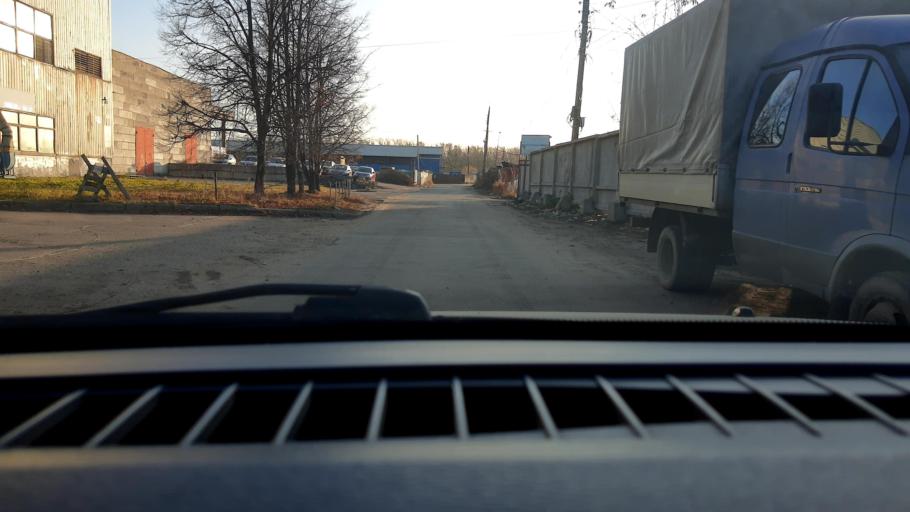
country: RU
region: Nizjnij Novgorod
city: Gorbatovka
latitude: 56.3183
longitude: 43.8574
